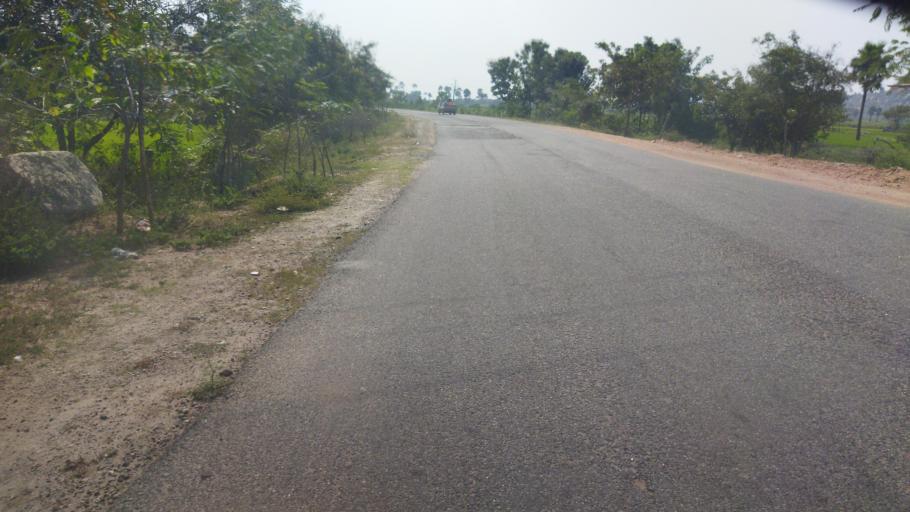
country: IN
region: Telangana
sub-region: Nalgonda
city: Nalgonda
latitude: 17.1097
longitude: 79.2788
